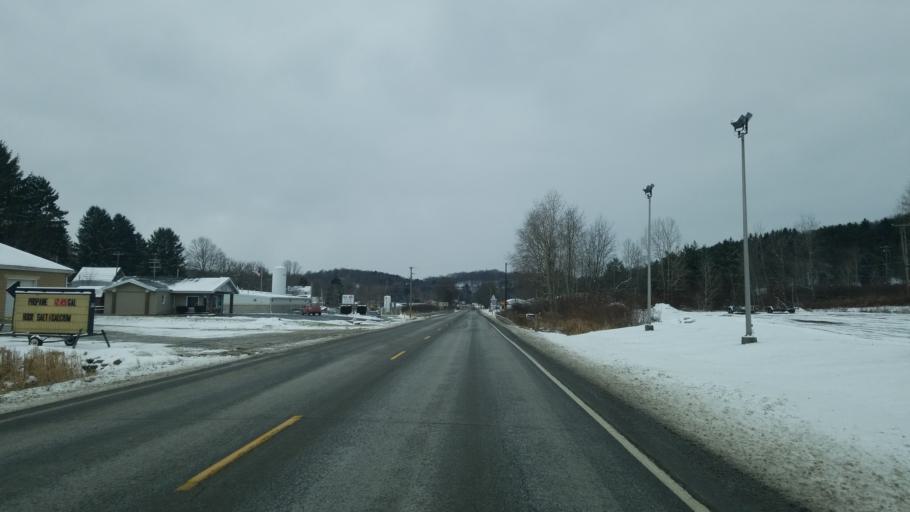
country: US
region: Pennsylvania
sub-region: Clearfield County
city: Sandy
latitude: 41.0862
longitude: -78.7654
